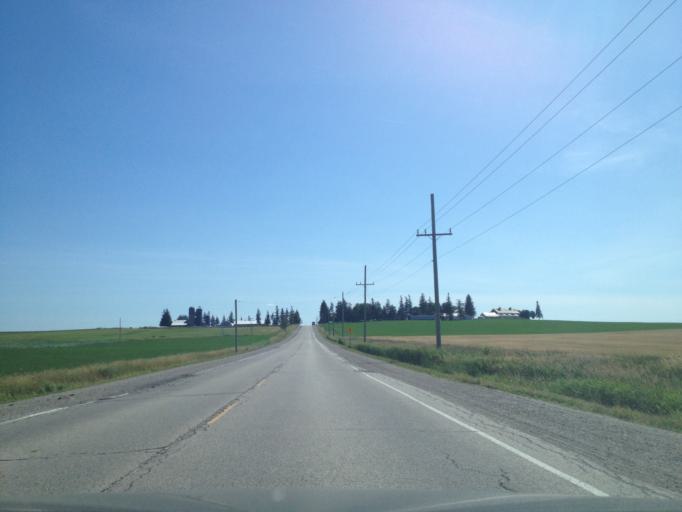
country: CA
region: Ontario
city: Waterloo
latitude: 43.5166
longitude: -80.7526
